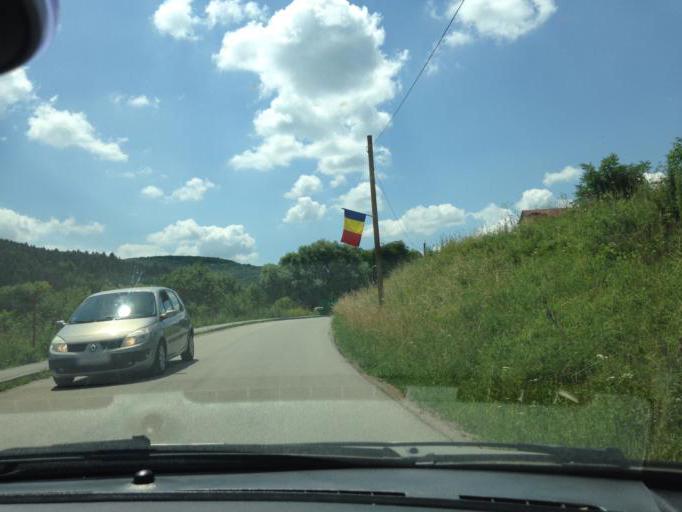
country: RO
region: Cluj
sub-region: Comuna Floresti
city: Floresti
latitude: 46.7486
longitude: 23.5339
